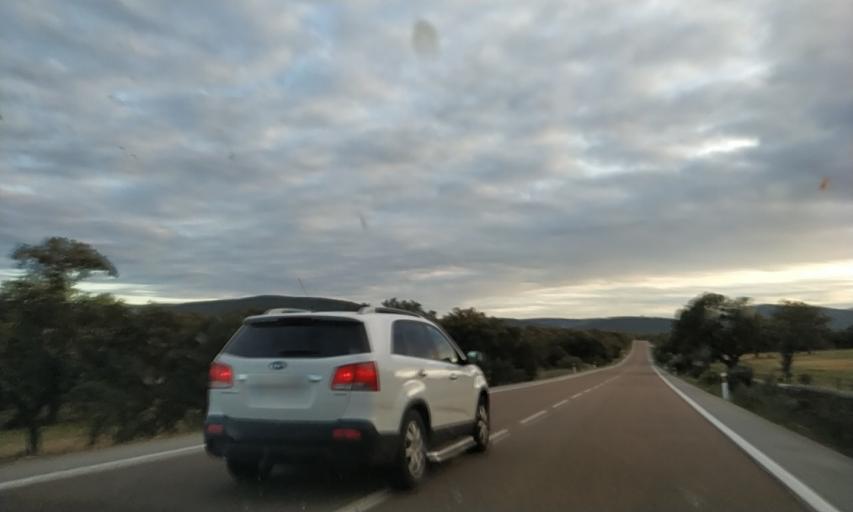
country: ES
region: Extremadura
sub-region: Provincia de Badajoz
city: Puebla de Obando
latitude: 39.2247
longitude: -6.5739
